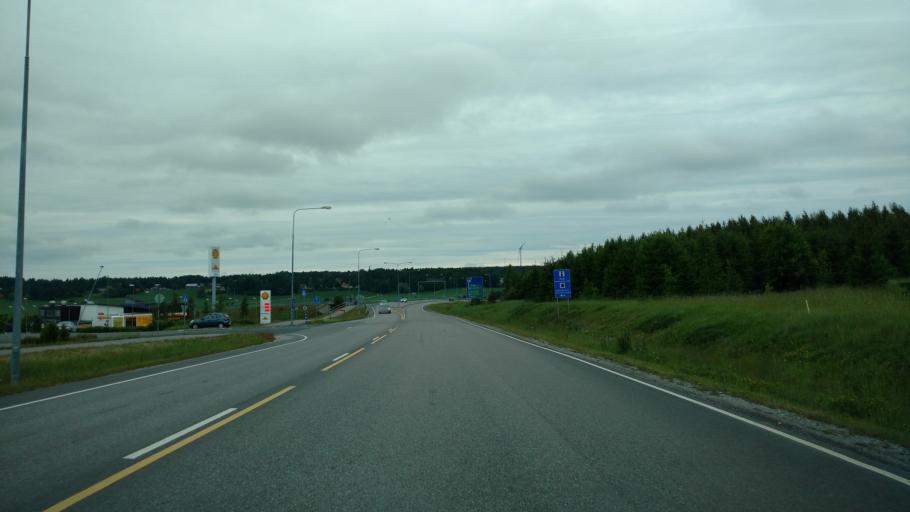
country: FI
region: Varsinais-Suomi
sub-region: Salo
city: Halikko
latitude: 60.4235
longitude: 23.0477
